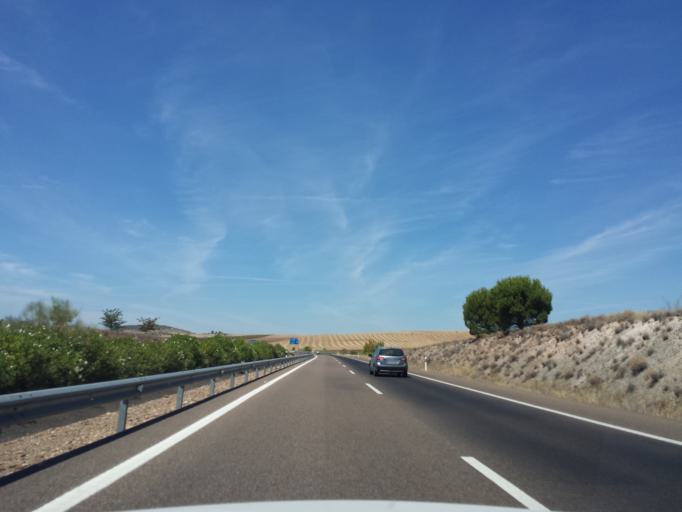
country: ES
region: Extremadura
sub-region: Provincia de Badajoz
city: Merida
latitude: 38.9459
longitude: -6.3135
